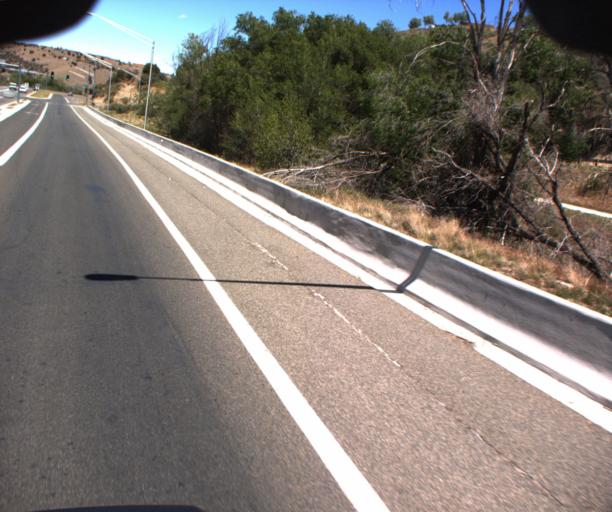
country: US
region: Arizona
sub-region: Yavapai County
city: Prescott
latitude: 34.5493
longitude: -112.4495
